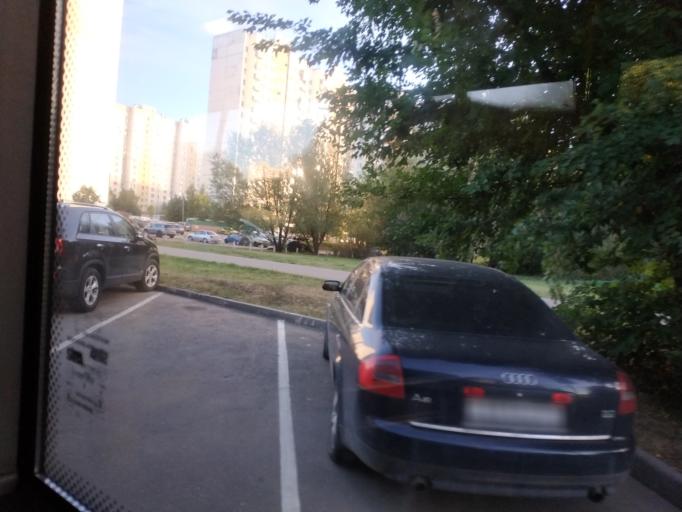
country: RU
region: Moscow
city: Novo-Peredelkino
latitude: 55.6434
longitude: 37.3551
